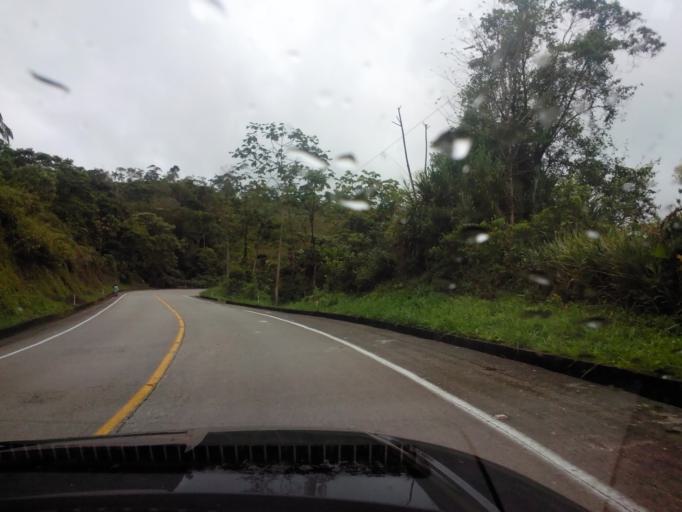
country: EC
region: Napo
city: Archidona
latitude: -0.7878
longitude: -77.7797
